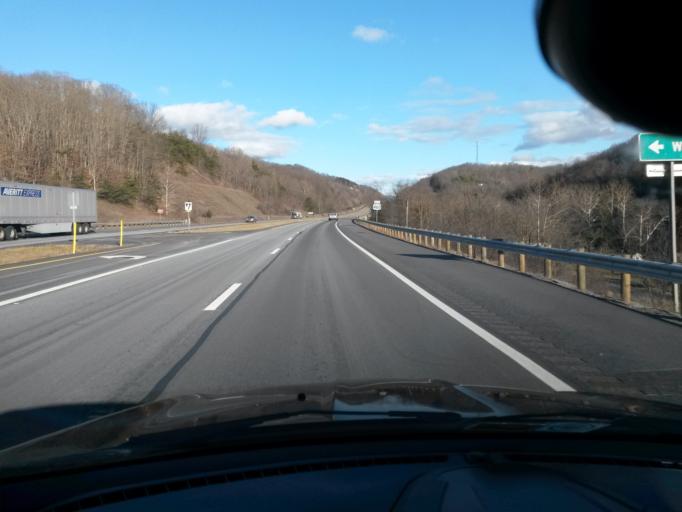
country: US
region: Virginia
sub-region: Giles County
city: Narrows
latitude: 37.3538
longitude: -80.9059
